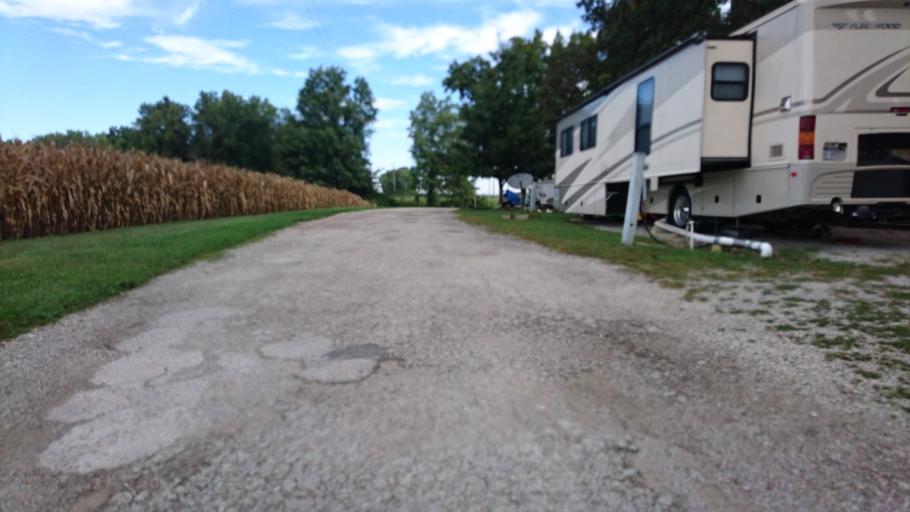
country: US
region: Illinois
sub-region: Macoupin County
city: Mount Olive
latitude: 38.9812
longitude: -89.6990
